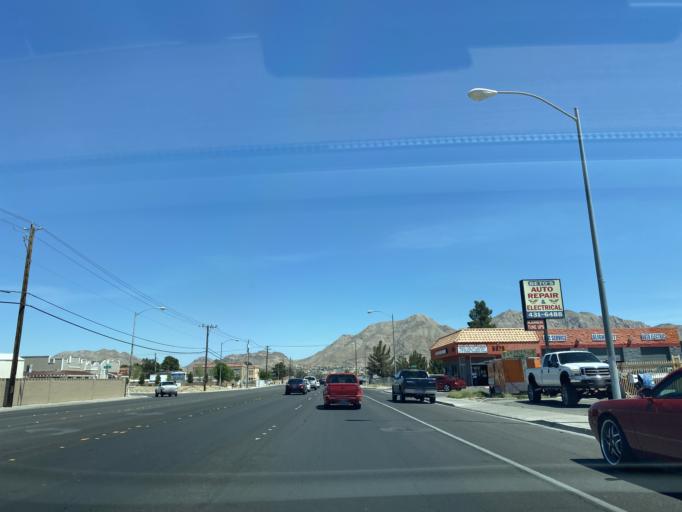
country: US
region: Nevada
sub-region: Clark County
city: Sunrise Manor
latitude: 36.1962
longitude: -115.0587
